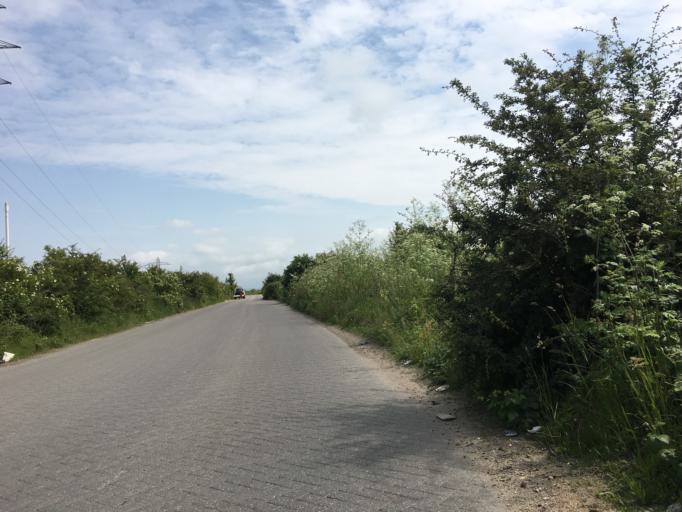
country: GB
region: England
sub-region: Kent
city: Queenborough
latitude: 51.3806
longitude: 0.7533
